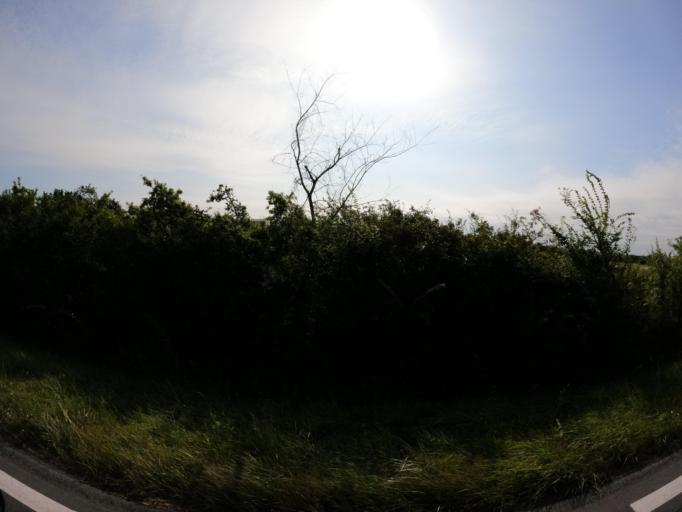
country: FR
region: Pays de la Loire
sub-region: Departement de la Vendee
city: Triaize
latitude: 46.3467
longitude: -1.2614
